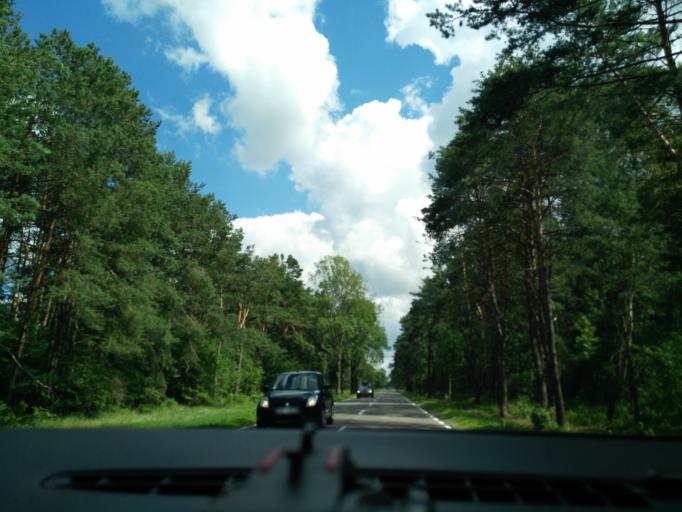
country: PL
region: Podlasie
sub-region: Powiat bielski
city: Bocki
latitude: 52.6367
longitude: 23.0244
